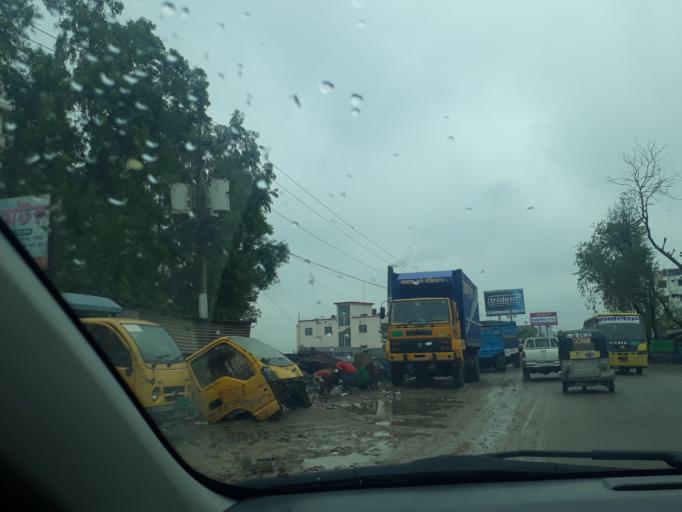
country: BD
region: Dhaka
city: Tungi
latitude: 23.8996
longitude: 90.3282
